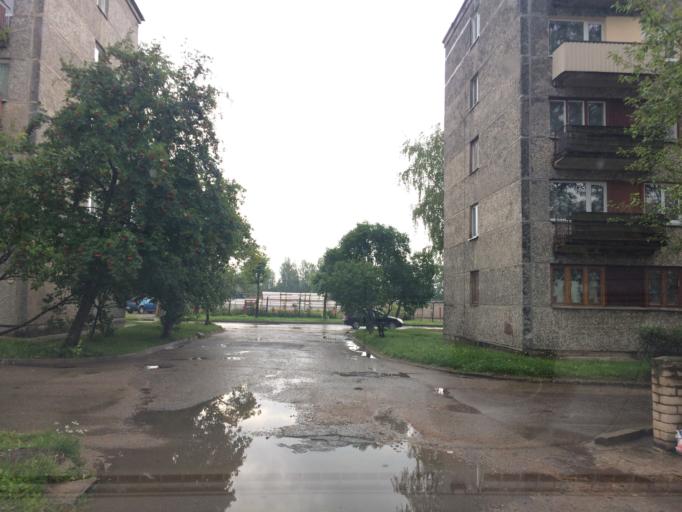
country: LV
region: Rezekne
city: Rezekne
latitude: 56.5241
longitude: 27.3519
